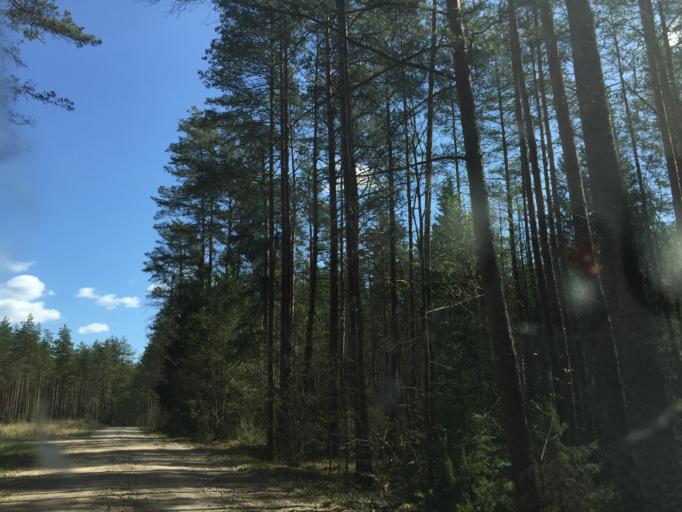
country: LV
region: Vecumnieki
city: Vecumnieki
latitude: 56.6507
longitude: 24.4847
